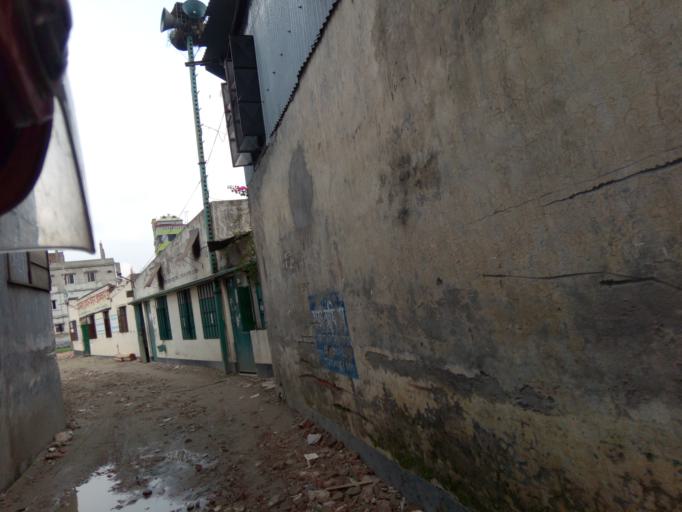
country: BD
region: Dhaka
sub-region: Dhaka
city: Dhaka
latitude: 23.7008
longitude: 90.4649
